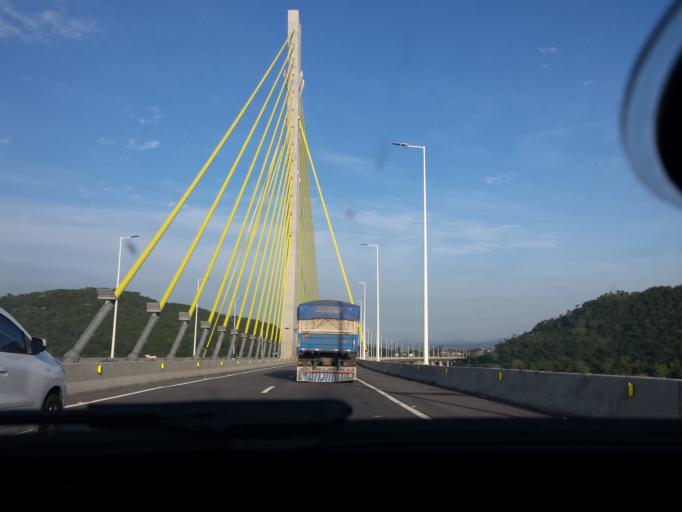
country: BR
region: Santa Catarina
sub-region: Laguna
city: Laguna
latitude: -28.4348
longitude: -48.8432
